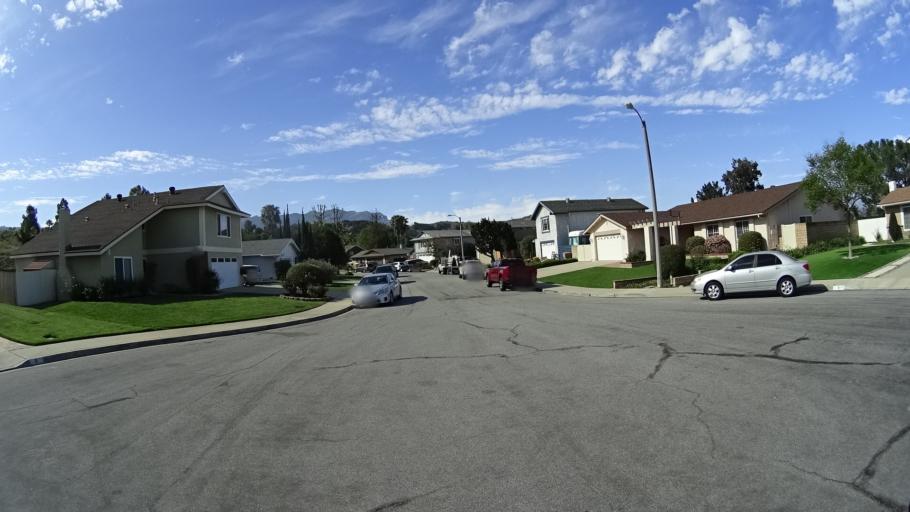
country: US
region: California
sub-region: Ventura County
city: Casa Conejo
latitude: 34.1766
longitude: -118.9442
